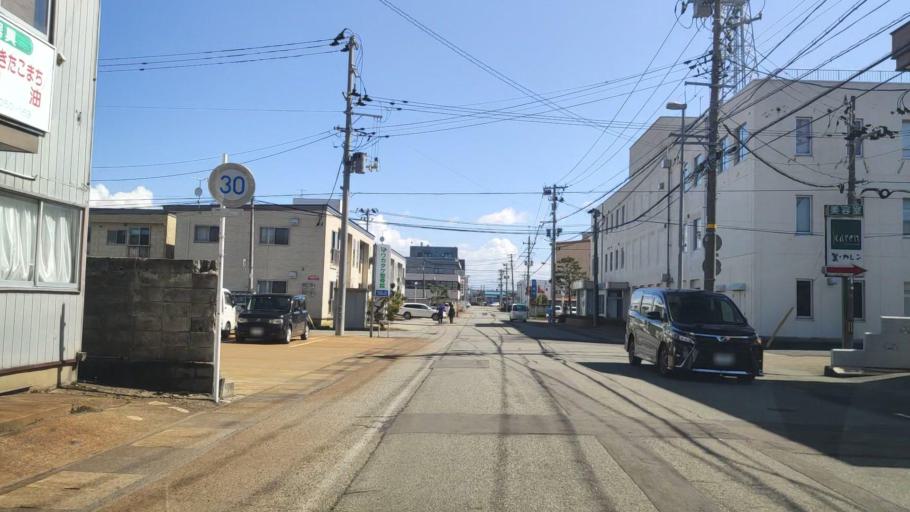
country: JP
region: Akita
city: Omagari
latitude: 39.4677
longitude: 140.4715
